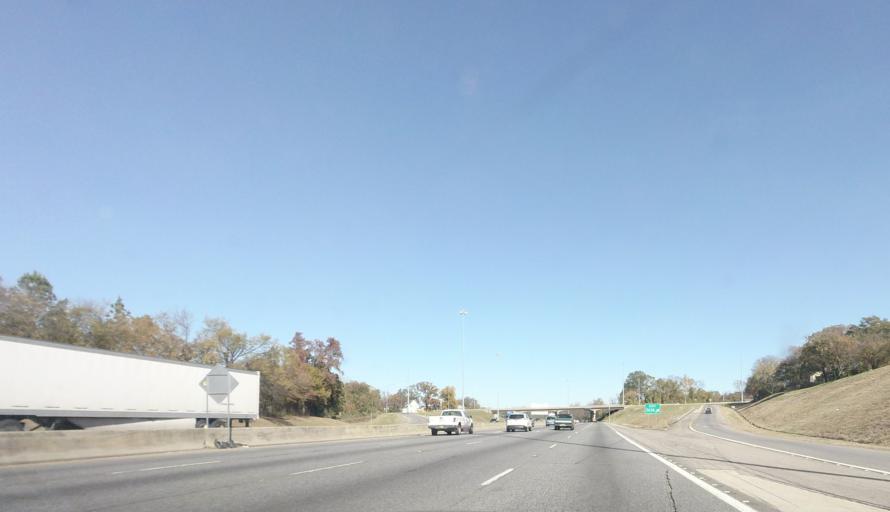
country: US
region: Alabama
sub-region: Jefferson County
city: Birmingham
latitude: 33.5302
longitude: -86.8254
